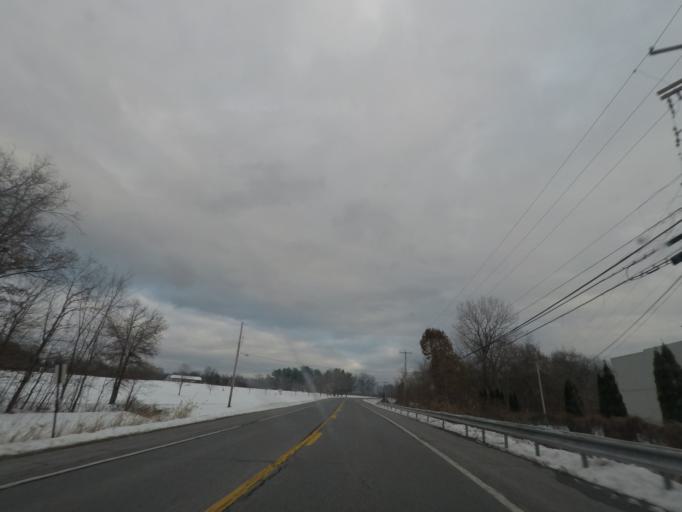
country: US
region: New York
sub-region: Ulster County
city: Plattekill
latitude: 41.6545
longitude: -74.1141
